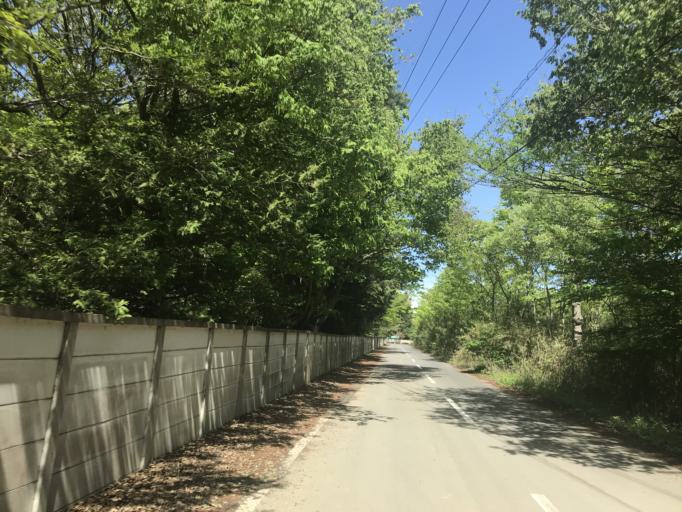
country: JP
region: Ibaraki
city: Shimodate
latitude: 36.2881
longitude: 140.0184
